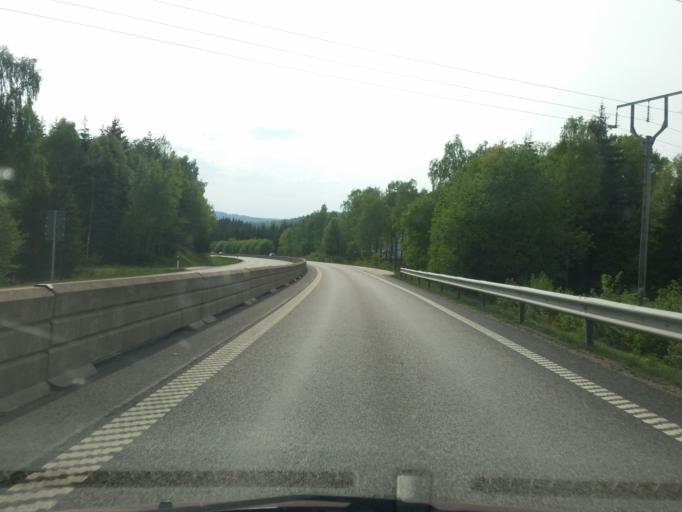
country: SE
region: Vaestra Goetaland
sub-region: Ulricehamns Kommun
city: Ulricehamn
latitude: 57.8101
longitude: 13.4394
